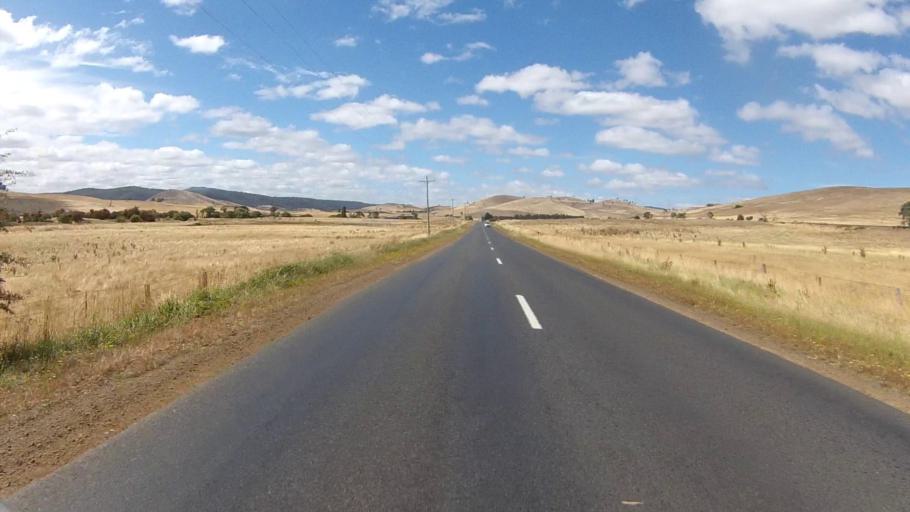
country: AU
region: Tasmania
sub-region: Brighton
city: Bridgewater
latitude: -42.5384
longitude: 147.3678
